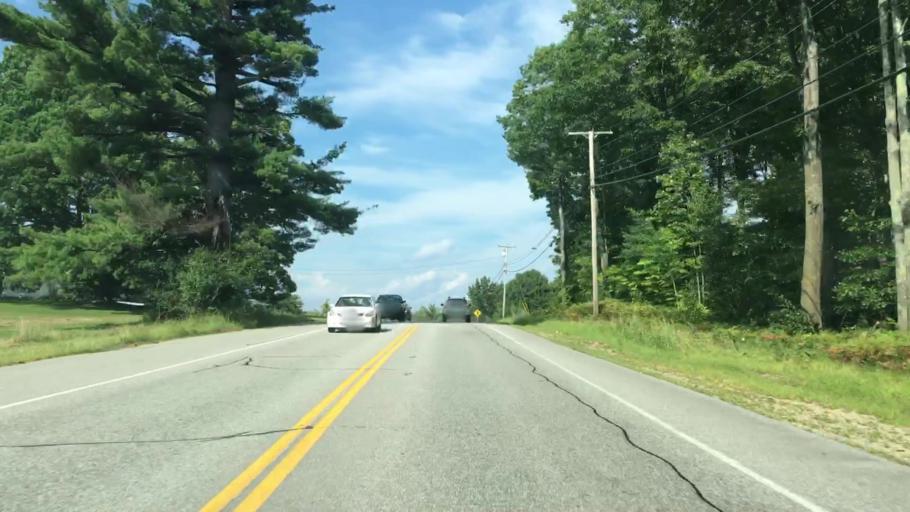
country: US
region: New Hampshire
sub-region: Belknap County
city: Sanbornton
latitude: 43.4702
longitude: -71.5450
